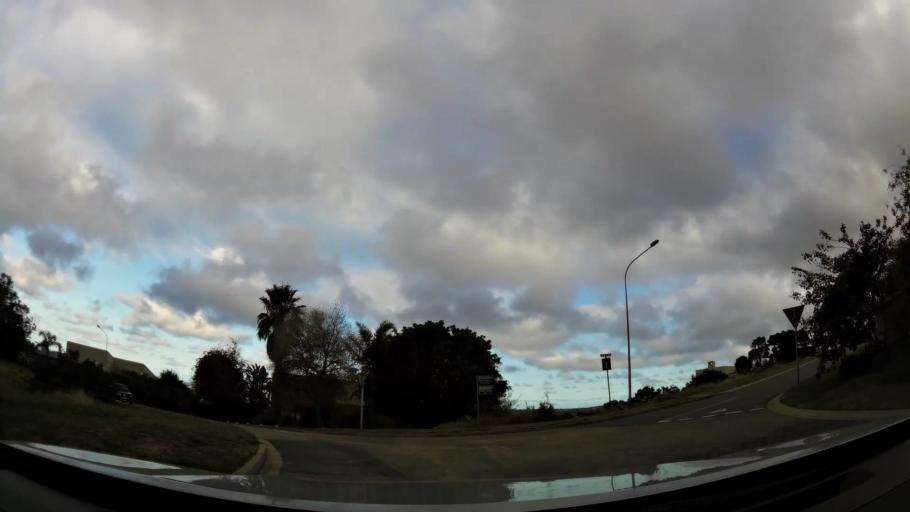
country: ZA
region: Western Cape
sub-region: Eden District Municipality
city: Plettenberg Bay
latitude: -34.0561
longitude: 23.3647
